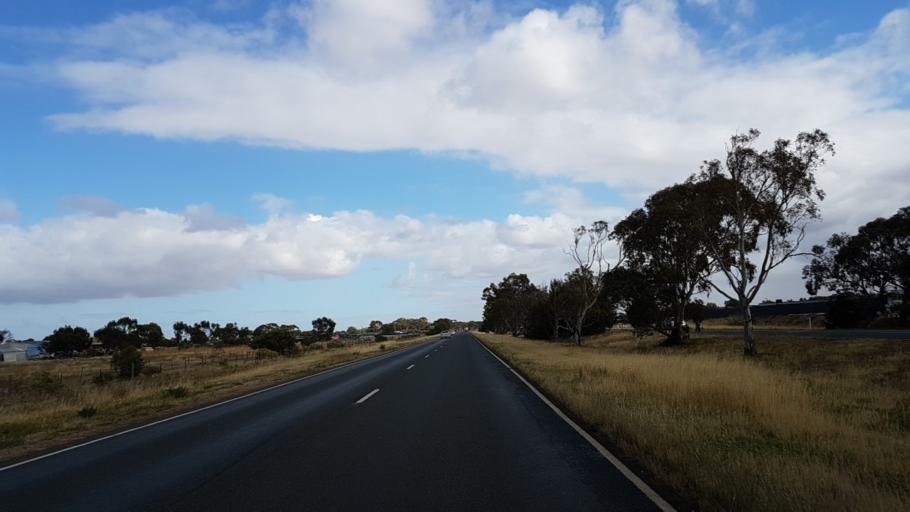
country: AU
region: South Australia
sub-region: Mallala
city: Two Wells
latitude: -34.6203
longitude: 138.5210
